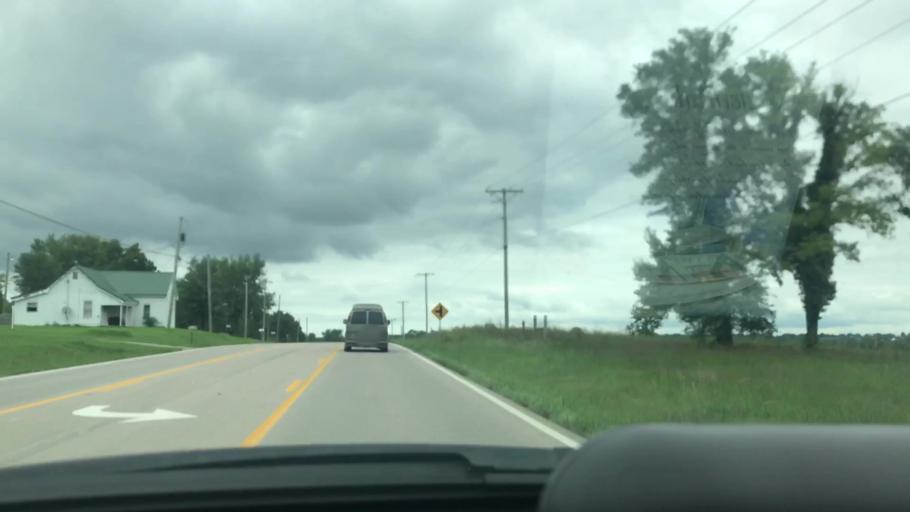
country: US
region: Missouri
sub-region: Dallas County
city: Buffalo
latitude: 37.6510
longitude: -93.1039
